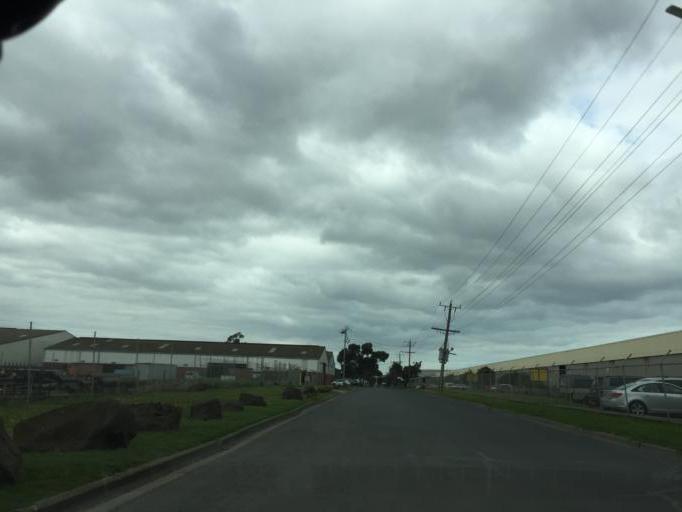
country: AU
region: Victoria
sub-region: Brimbank
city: Brooklyn
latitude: -37.8023
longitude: 144.8481
